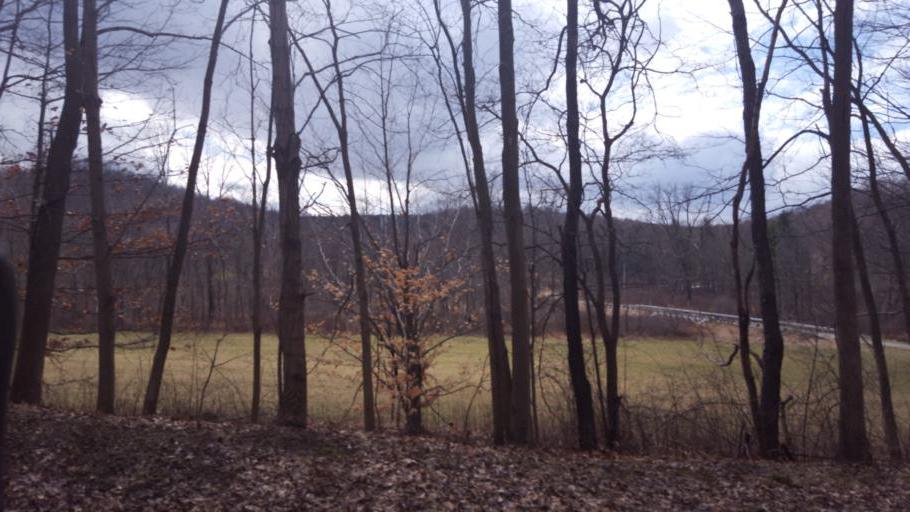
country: US
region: Ohio
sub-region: Sandusky County
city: Bellville
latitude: 40.6395
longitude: -82.4648
